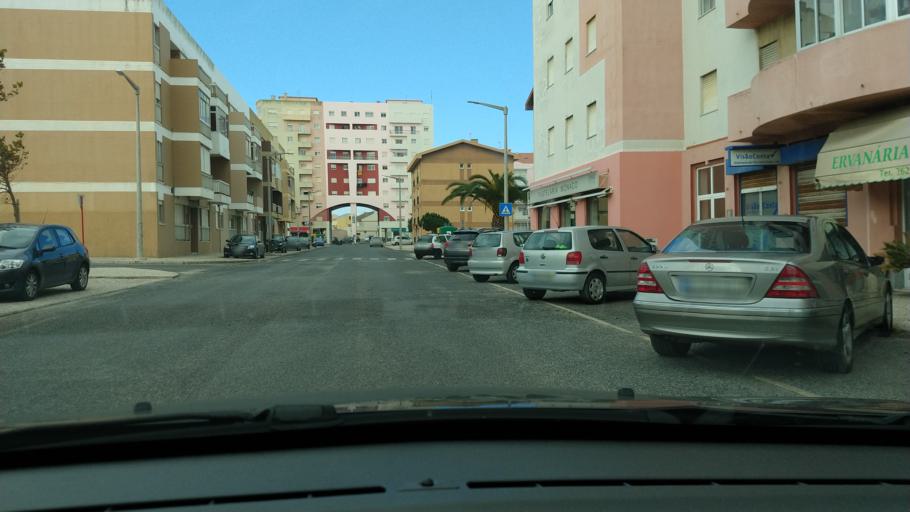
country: PT
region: Leiria
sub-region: Peniche
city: Peniche
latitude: 39.3619
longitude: -9.3889
